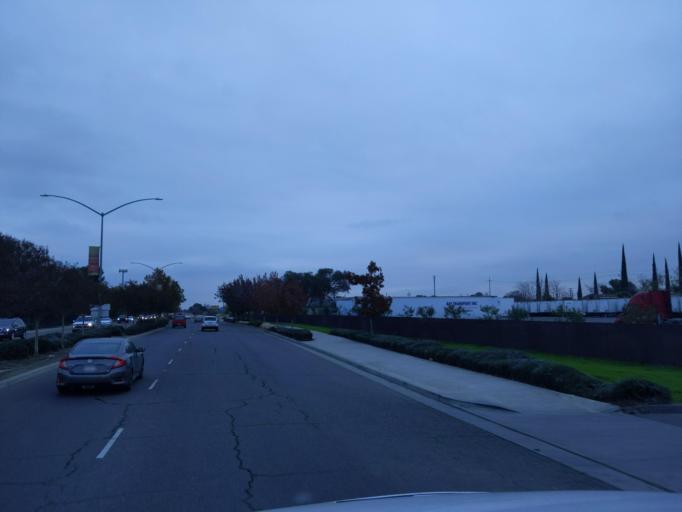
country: US
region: California
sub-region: San Joaquin County
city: Kennedy
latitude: 37.9386
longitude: -121.2697
